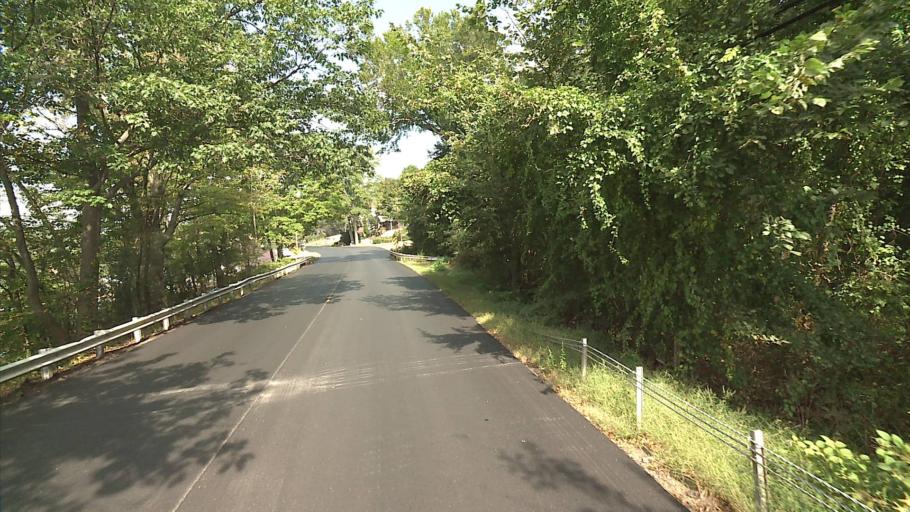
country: US
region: Connecticut
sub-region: Fairfield County
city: Shelton
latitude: 41.3442
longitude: -73.1223
